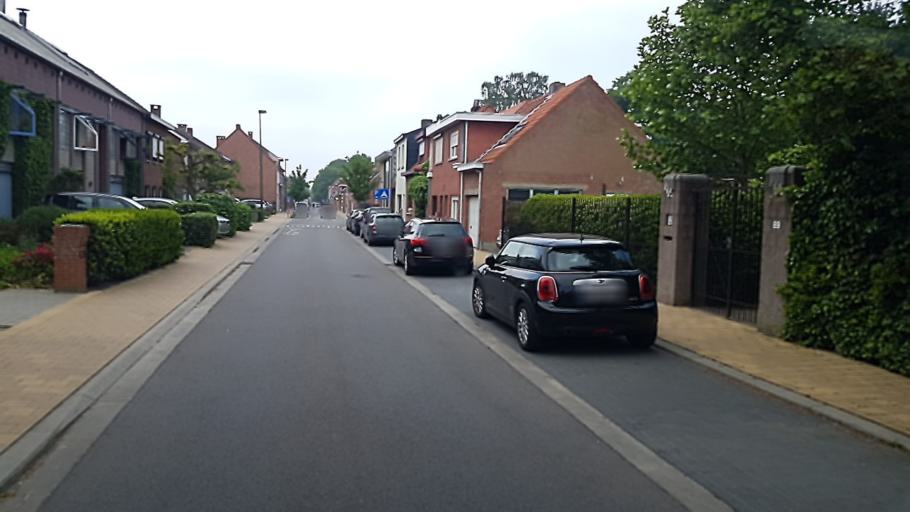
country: BE
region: Flanders
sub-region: Provincie Antwerpen
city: Kapellen
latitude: 51.3224
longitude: 4.4303
